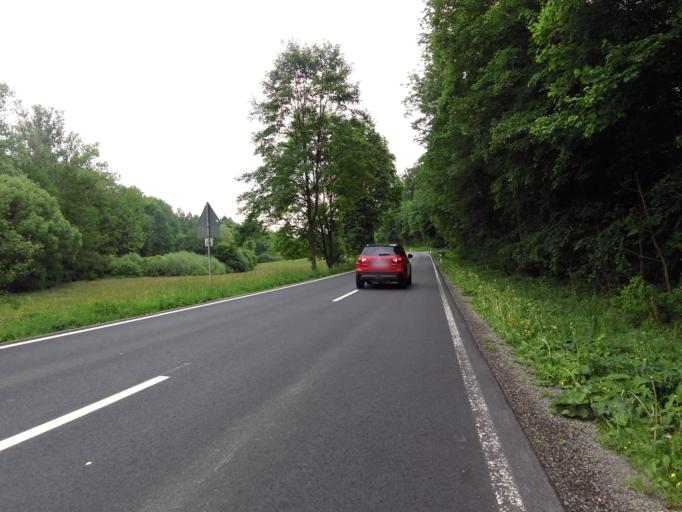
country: DE
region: Bavaria
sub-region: Regierungsbezirk Unterfranken
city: Wuerzburg
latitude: 49.7376
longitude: 9.8700
